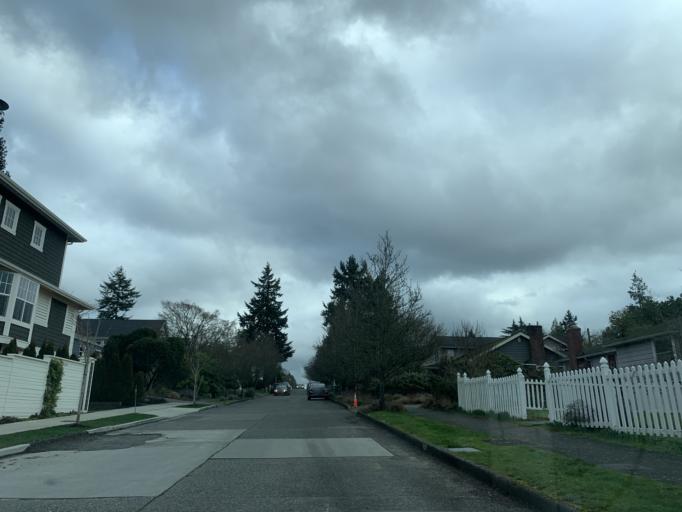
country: US
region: Washington
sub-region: King County
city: Yarrow Point
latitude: 47.6721
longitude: -122.2662
